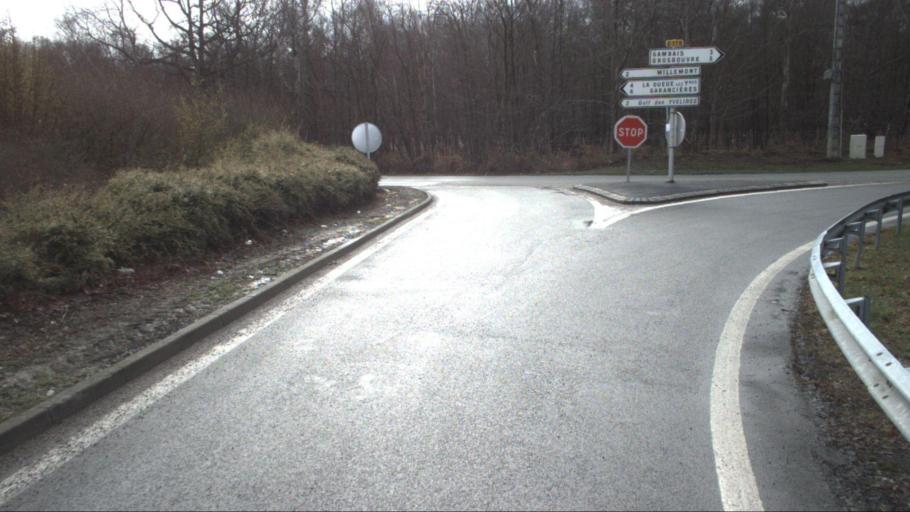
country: FR
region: Ile-de-France
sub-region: Departement des Yvelines
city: Orgerus
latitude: 48.7983
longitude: 1.7093
